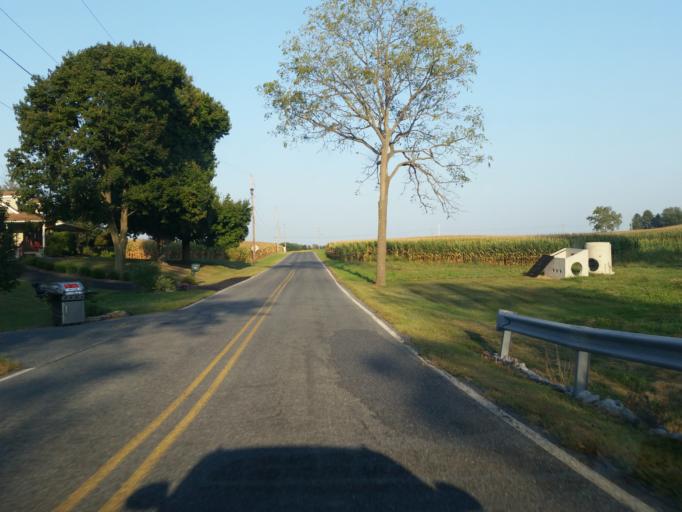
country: US
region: Pennsylvania
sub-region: Lebanon County
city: Cleona
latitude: 40.3632
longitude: -76.4979
